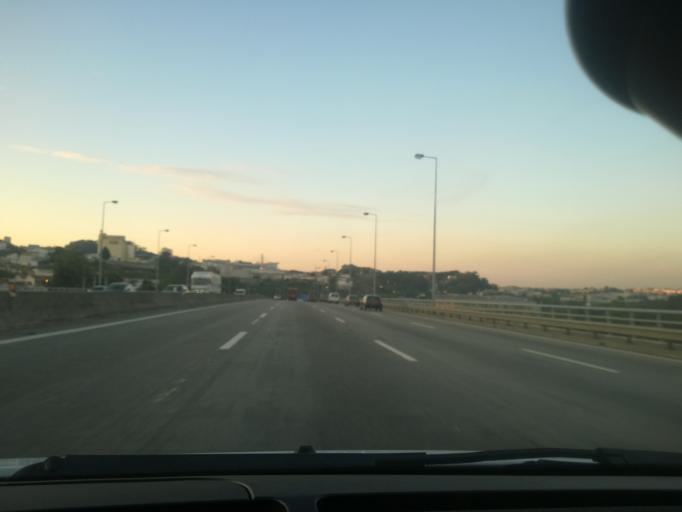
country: PT
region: Porto
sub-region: Vila Nova de Gaia
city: Oliveira do Douro
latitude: 41.1424
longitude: -8.5808
